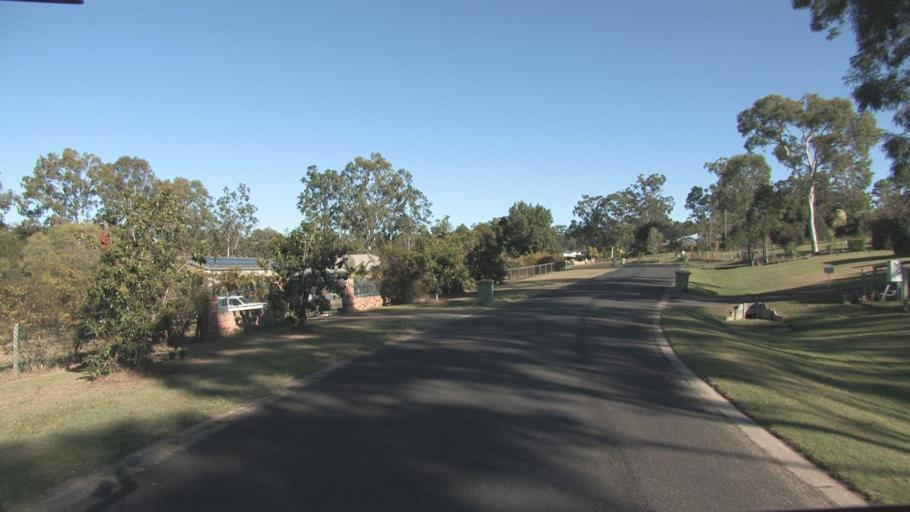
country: AU
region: Queensland
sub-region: Logan
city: North Maclean
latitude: -27.7447
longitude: 152.9620
